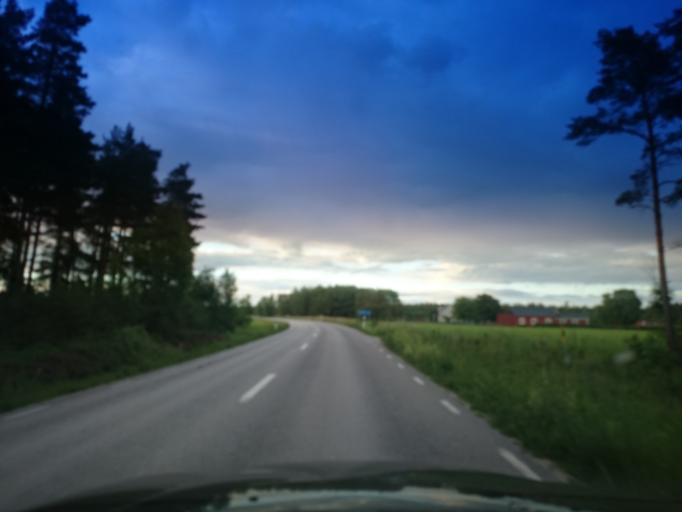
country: SE
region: Gotland
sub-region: Gotland
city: Vibble
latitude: 57.4988
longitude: 18.3710
